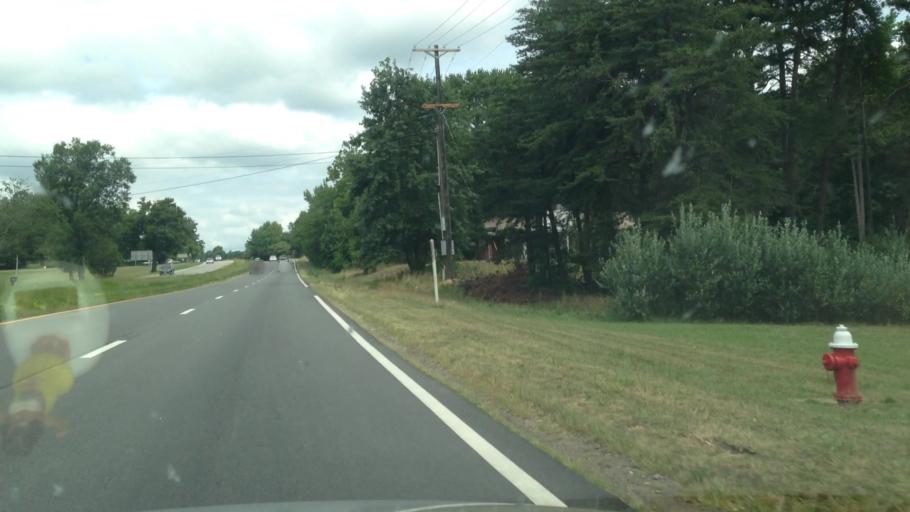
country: US
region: Virginia
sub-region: Pittsylvania County
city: Mount Hermon
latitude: 36.7084
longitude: -79.3740
